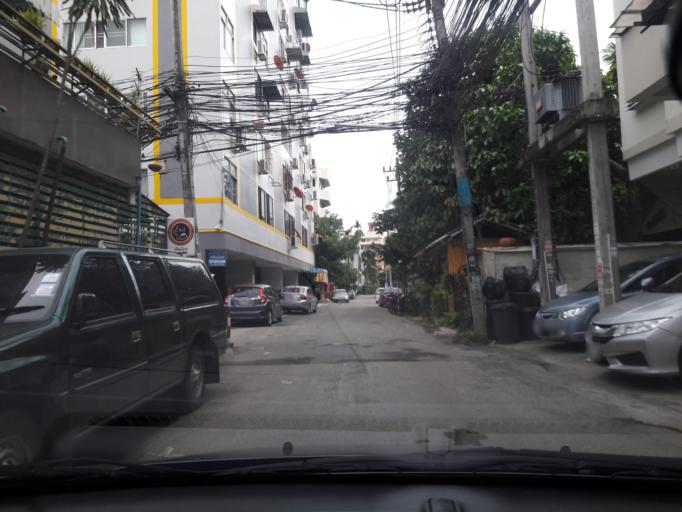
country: TH
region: Chiang Mai
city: Chiang Mai
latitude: 18.7879
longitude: 98.9724
